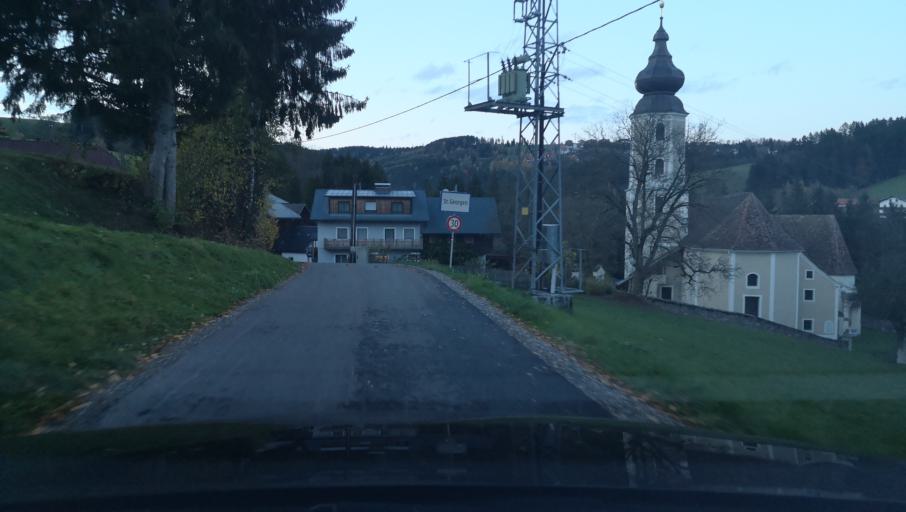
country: AT
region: Styria
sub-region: Politischer Bezirk Weiz
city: Birkfeld
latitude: 47.3391
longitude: 15.6836
